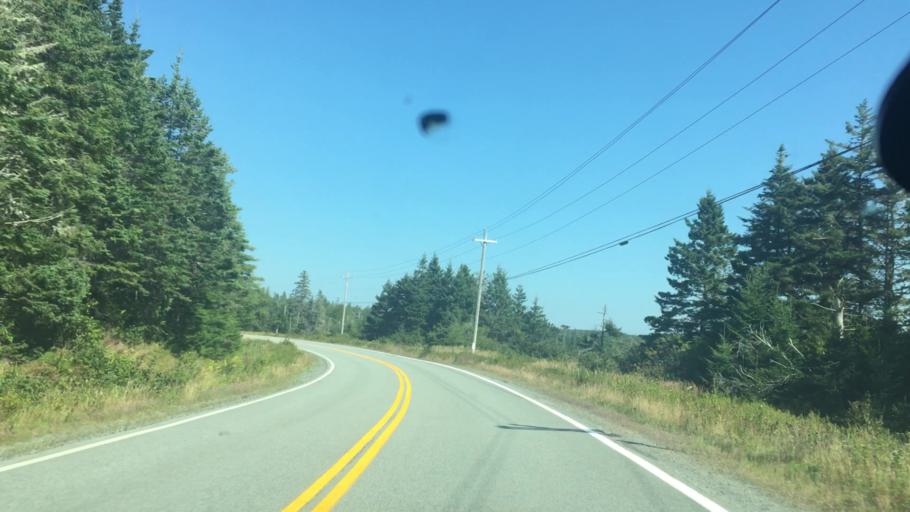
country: CA
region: Nova Scotia
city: New Glasgow
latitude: 44.9243
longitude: -62.2984
